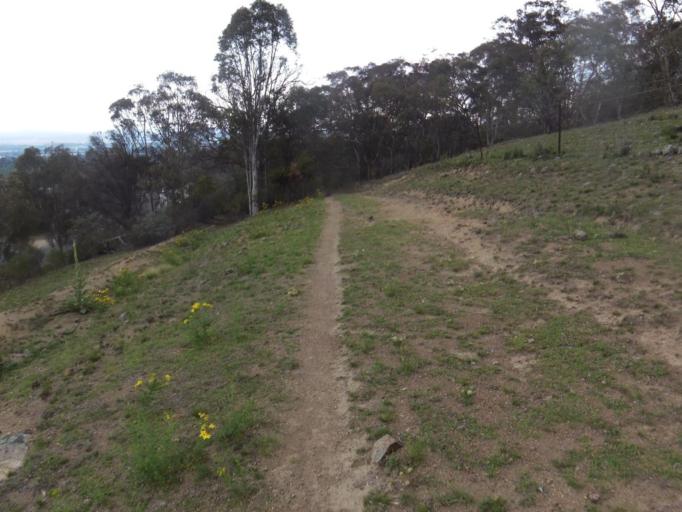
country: AU
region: Australian Capital Territory
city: Forrest
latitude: -35.3477
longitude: 149.1265
